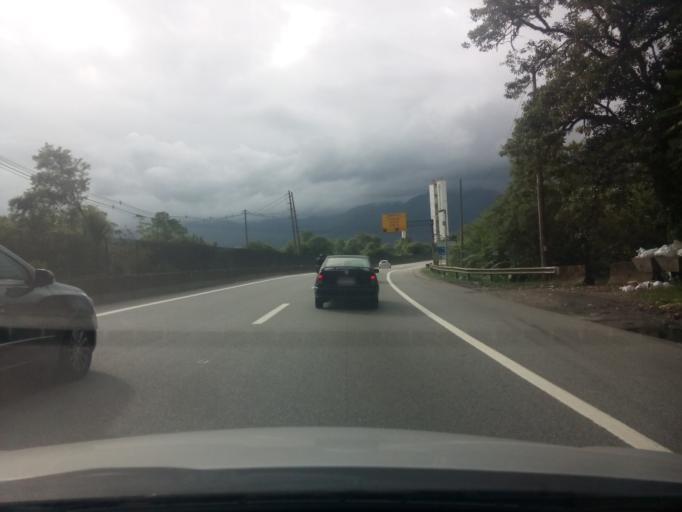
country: BR
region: Sao Paulo
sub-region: Cubatao
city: Cubatao
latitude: -23.8572
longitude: -46.3678
